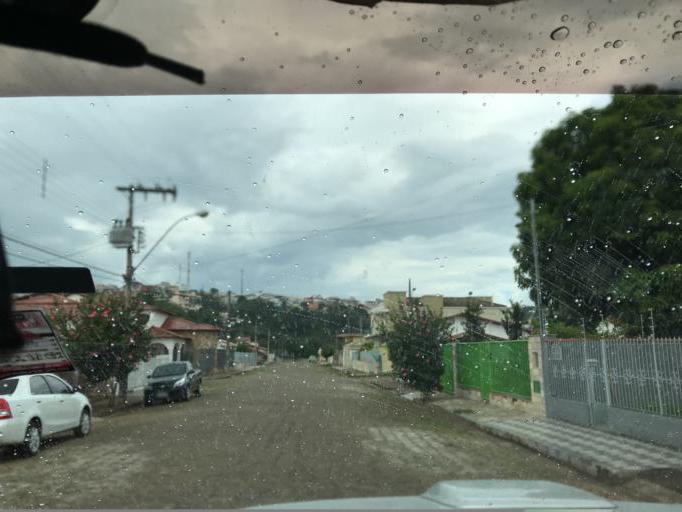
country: BR
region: Minas Gerais
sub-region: Tres Coracoes
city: Tres Coracoes
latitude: -21.7012
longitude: -45.2506
